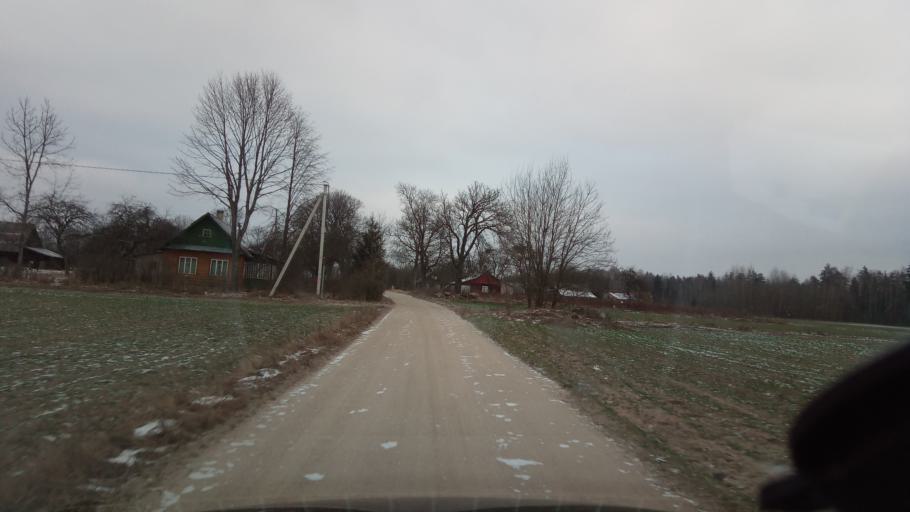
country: LT
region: Alytaus apskritis
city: Varena
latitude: 54.1262
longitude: 24.7052
